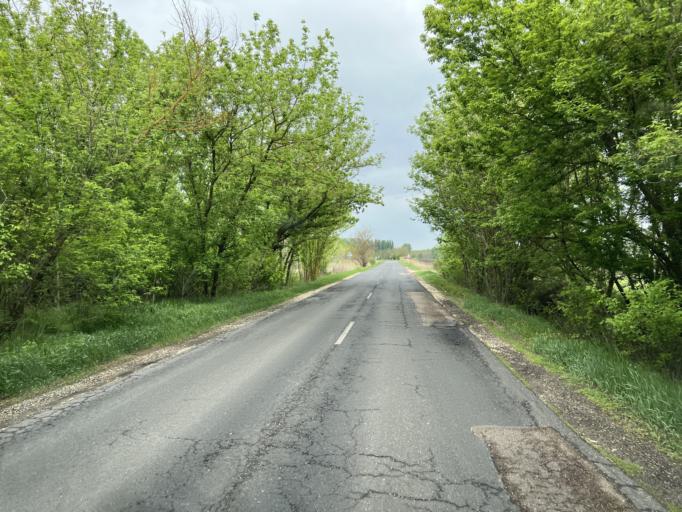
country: HU
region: Pest
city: Farmos
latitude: 47.3942
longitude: 19.8919
